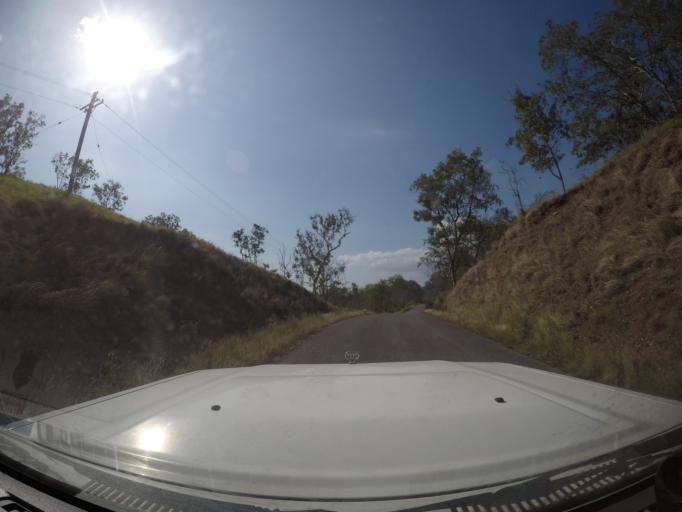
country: PG
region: Central Province
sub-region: Rigo
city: Kwikila
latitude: -9.8680
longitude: 147.5637
